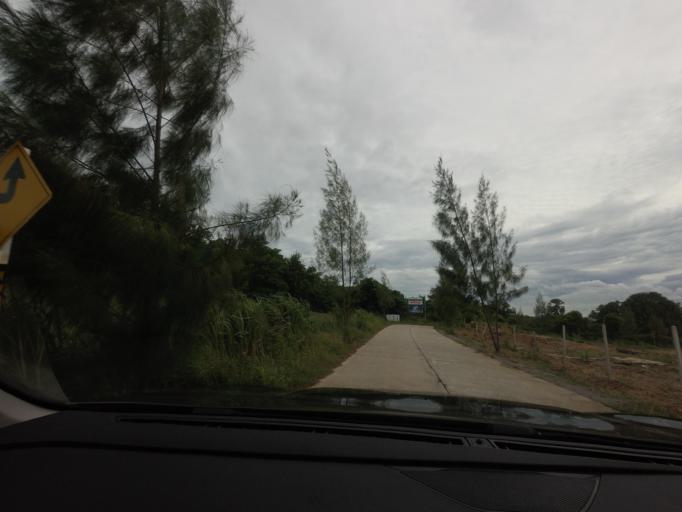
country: TH
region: Prachuap Khiri Khan
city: Hua Hin
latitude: 12.4866
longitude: 99.9423
